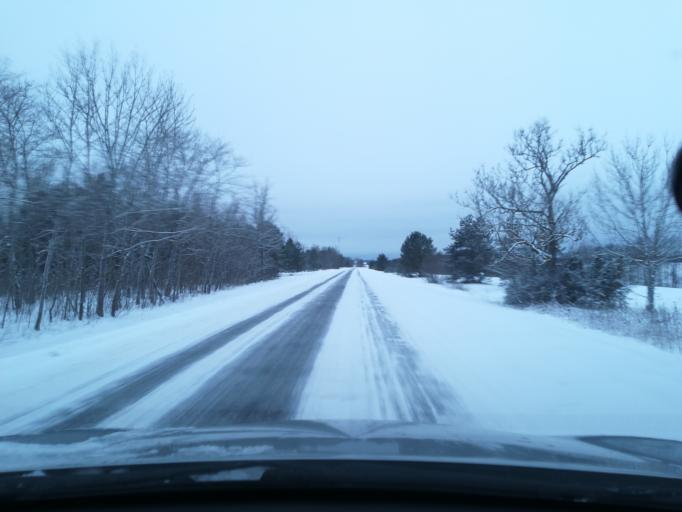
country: EE
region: Harju
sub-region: Keila linn
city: Keila
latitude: 59.3661
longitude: 24.3294
